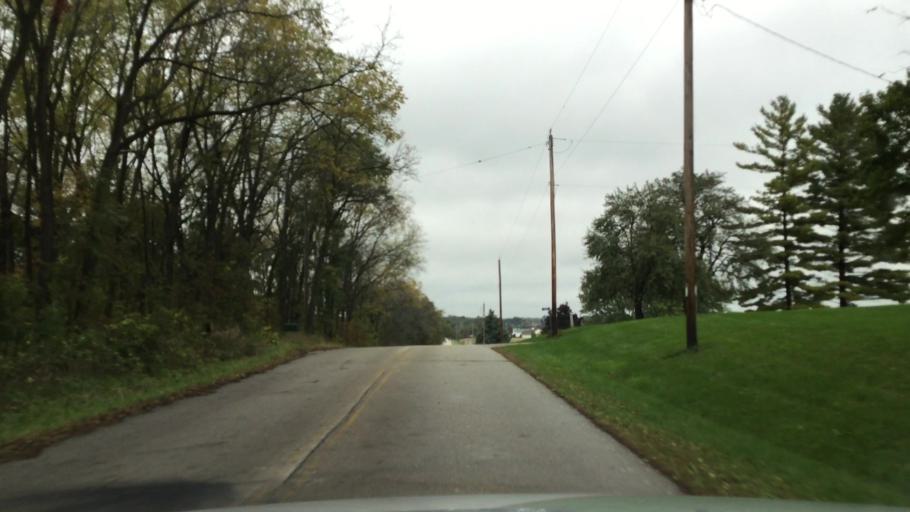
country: US
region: Wisconsin
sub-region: Racine County
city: Eagle Lake
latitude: 42.7489
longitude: -88.1553
